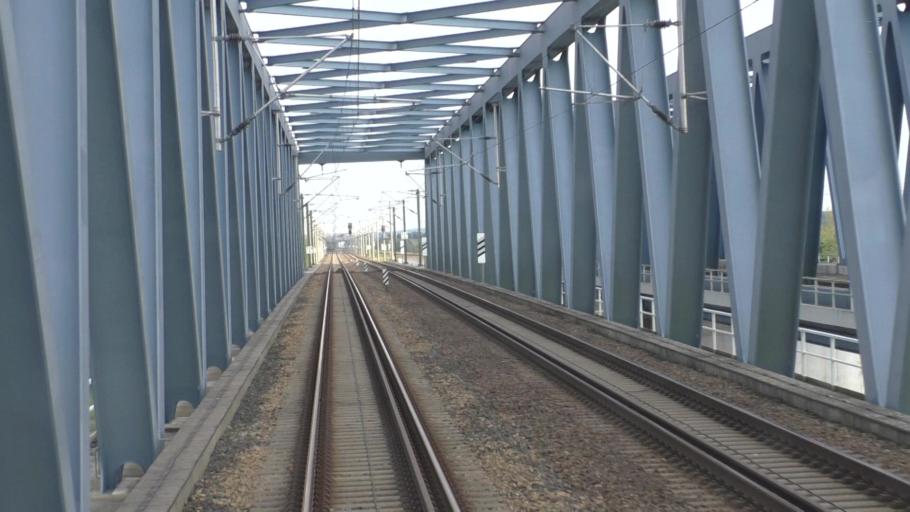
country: DE
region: Saxony-Anhalt
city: Schonhausen
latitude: 52.5973
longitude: 12.0019
